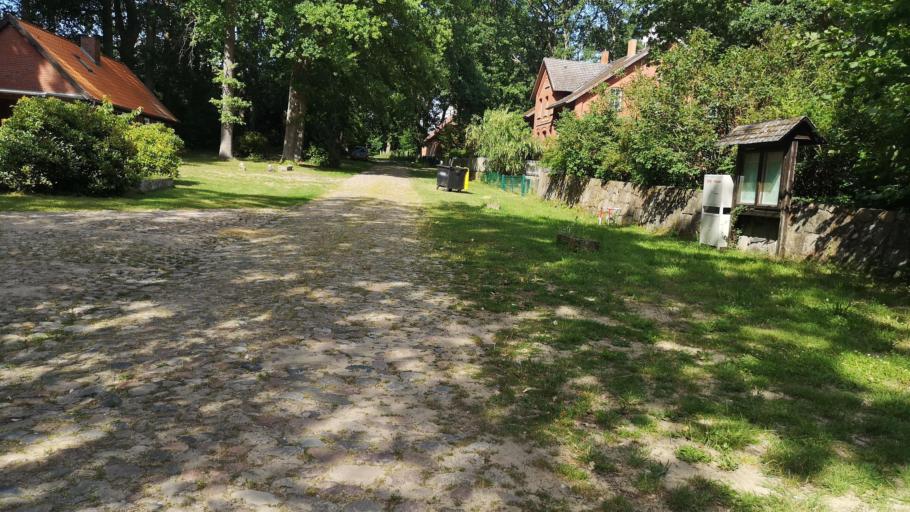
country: DE
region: Lower Saxony
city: Thomasburg
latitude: 53.2226
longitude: 10.6751
